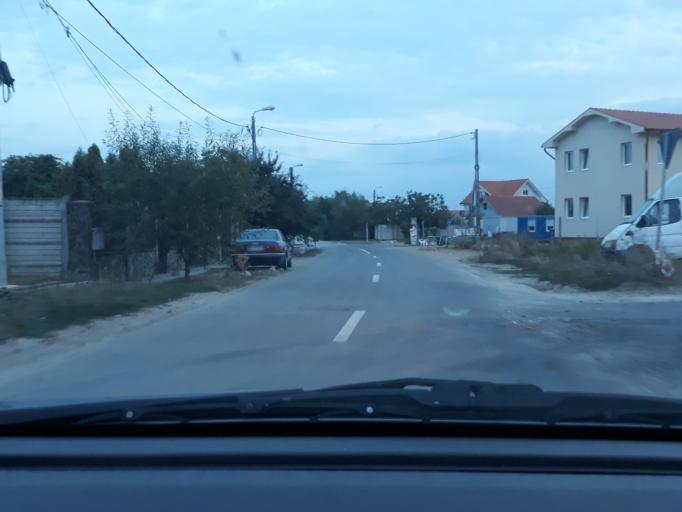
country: RO
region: Bihor
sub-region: Comuna Biharea
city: Oradea
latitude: 47.0267
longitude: 21.9355
